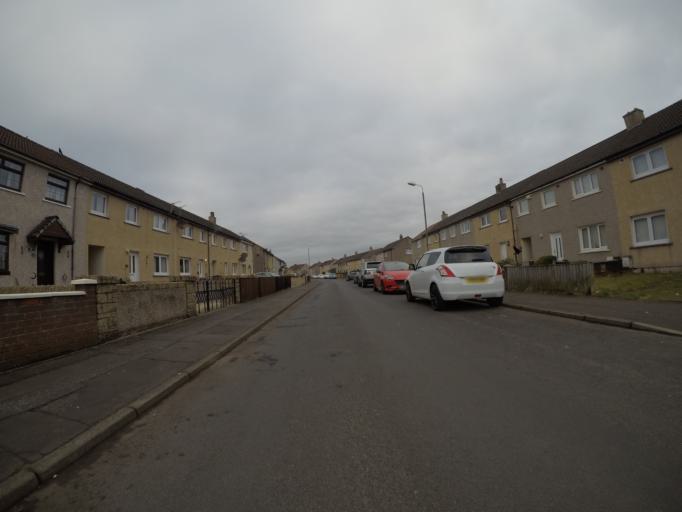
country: GB
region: Scotland
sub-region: North Ayrshire
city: Irvine
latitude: 55.6254
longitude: -4.6665
